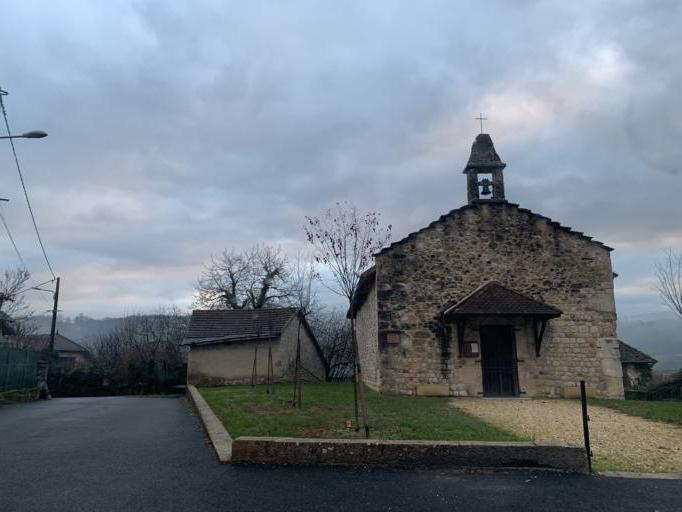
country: FR
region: Rhone-Alpes
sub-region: Departement de l'Ain
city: Belley
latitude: 45.7763
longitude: 5.6854
